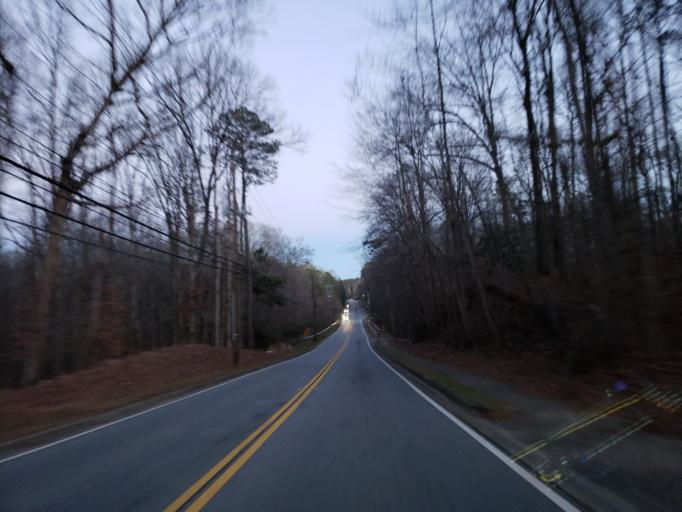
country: US
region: Georgia
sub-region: Cobb County
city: Kennesaw
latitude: 33.9656
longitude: -84.6943
